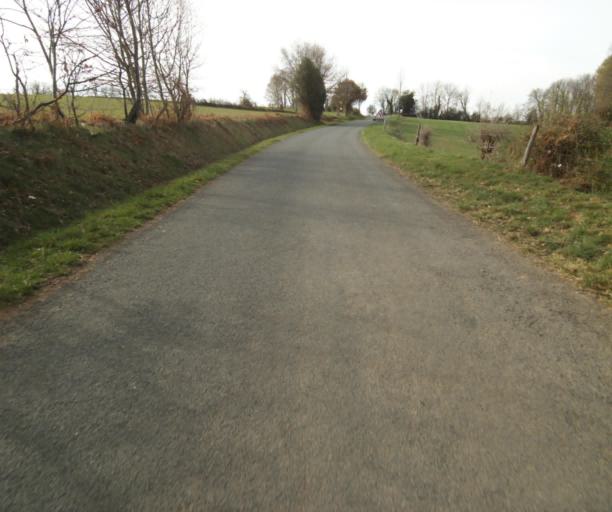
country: FR
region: Limousin
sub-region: Departement de la Correze
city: Chamboulive
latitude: 45.4158
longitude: 1.7839
